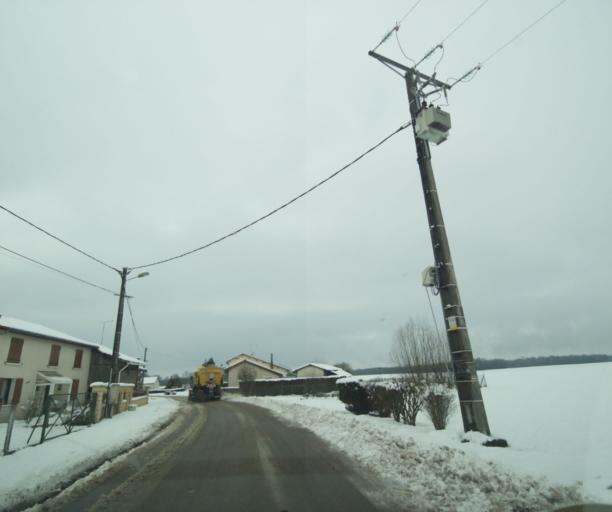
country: FR
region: Champagne-Ardenne
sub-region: Departement de la Haute-Marne
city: Montier-en-Der
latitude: 48.4906
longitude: 4.6956
